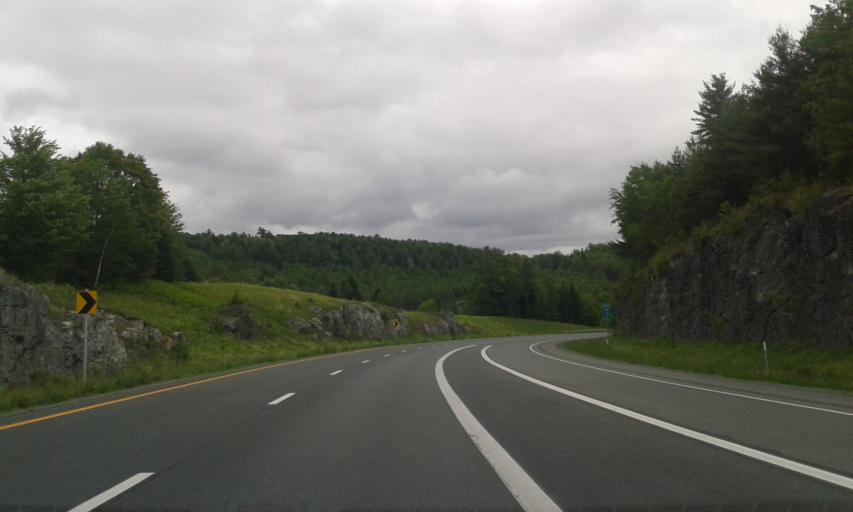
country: US
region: New Hampshire
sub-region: Grafton County
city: Littleton
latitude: 44.3252
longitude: -71.8007
